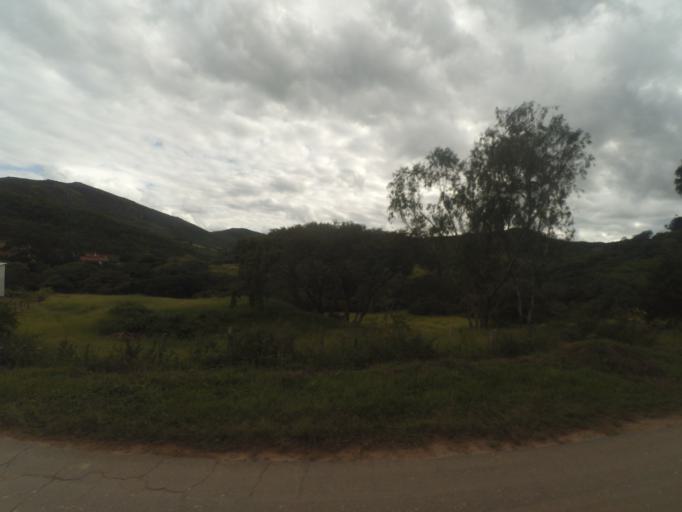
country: BO
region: Santa Cruz
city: Samaipata
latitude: -18.1699
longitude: -63.8327
